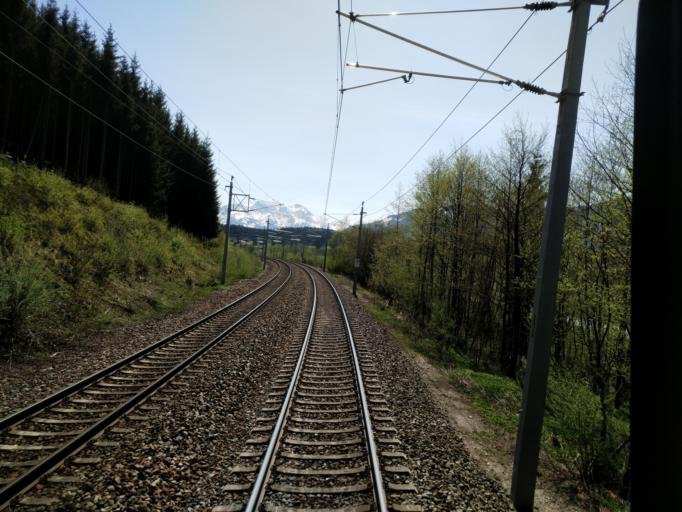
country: AT
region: Salzburg
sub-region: Politischer Bezirk Zell am See
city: Saalfelden am Steinernen Meer
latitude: 47.4141
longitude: 12.8277
